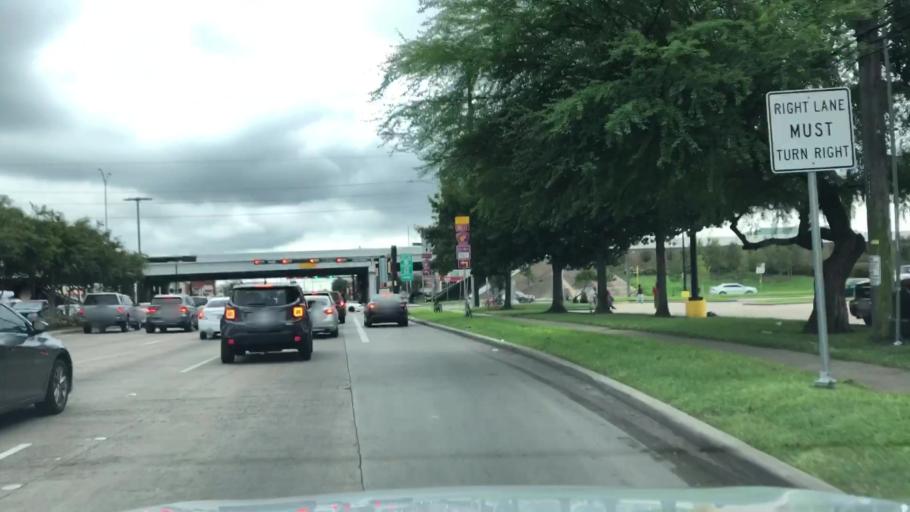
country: US
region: Texas
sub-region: Fort Bend County
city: Meadows Place
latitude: 29.7043
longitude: -95.5588
